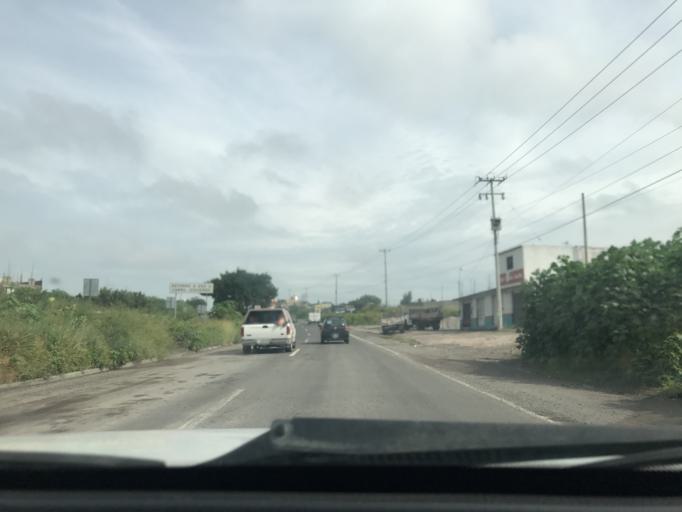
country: MX
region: Morelos
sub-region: Yecapixtla
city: Juan Morales
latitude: 18.8072
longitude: -98.9153
